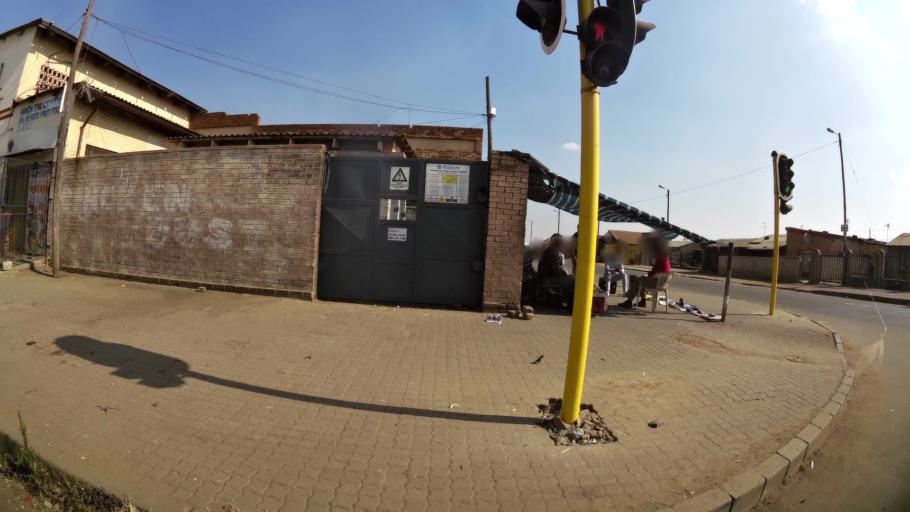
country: ZA
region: Gauteng
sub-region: Ekurhuleni Metropolitan Municipality
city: Brakpan
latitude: -26.1405
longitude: 28.4234
